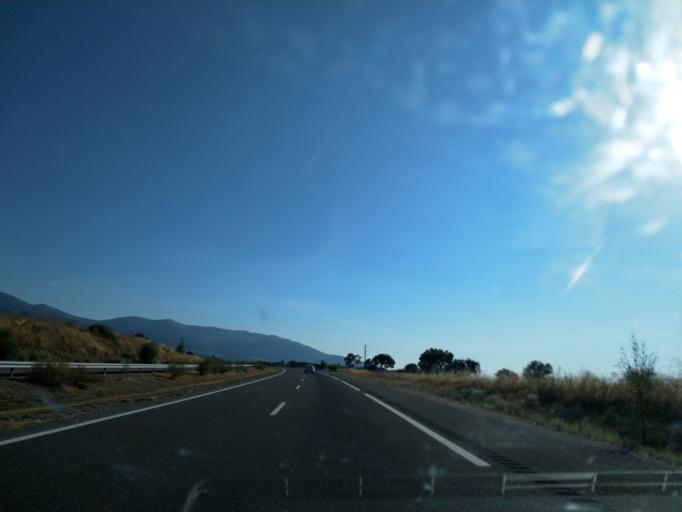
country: ES
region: Castille and Leon
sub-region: Provincia de Segovia
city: Segovia
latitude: 40.8920
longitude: -4.1140
